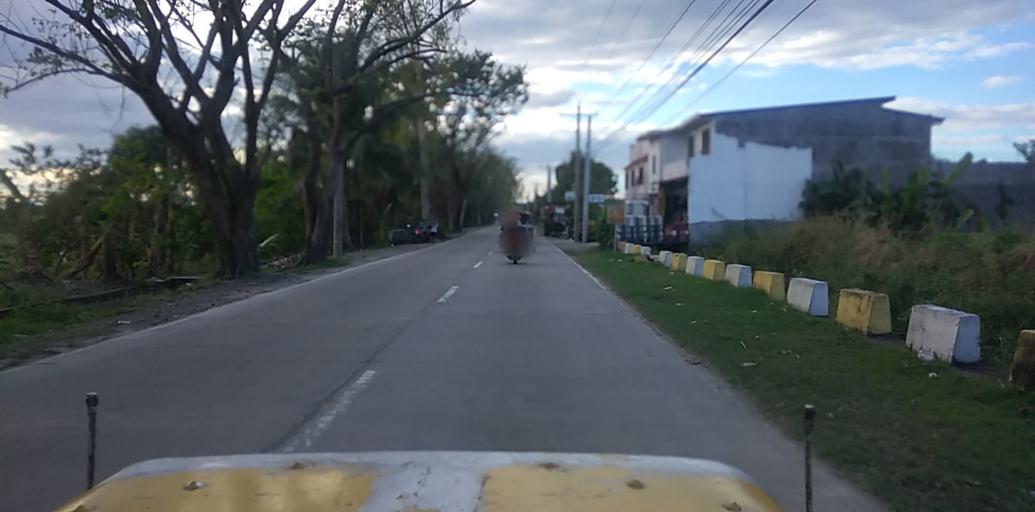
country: PH
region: Central Luzon
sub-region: Province of Pampanga
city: Arayat
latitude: 15.1495
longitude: 120.7549
